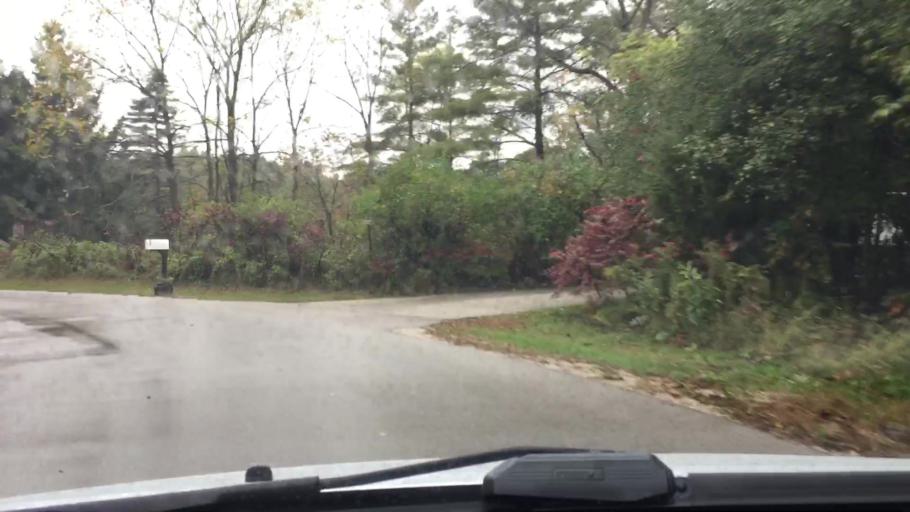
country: US
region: Wisconsin
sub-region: Waukesha County
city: North Prairie
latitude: 42.9313
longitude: -88.4530
